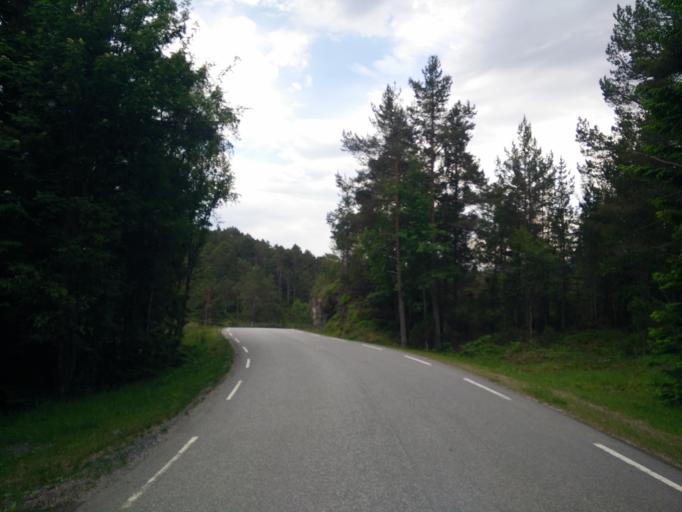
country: NO
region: More og Romsdal
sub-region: Kristiansund
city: Rensvik
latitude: 63.0330
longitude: 7.9541
